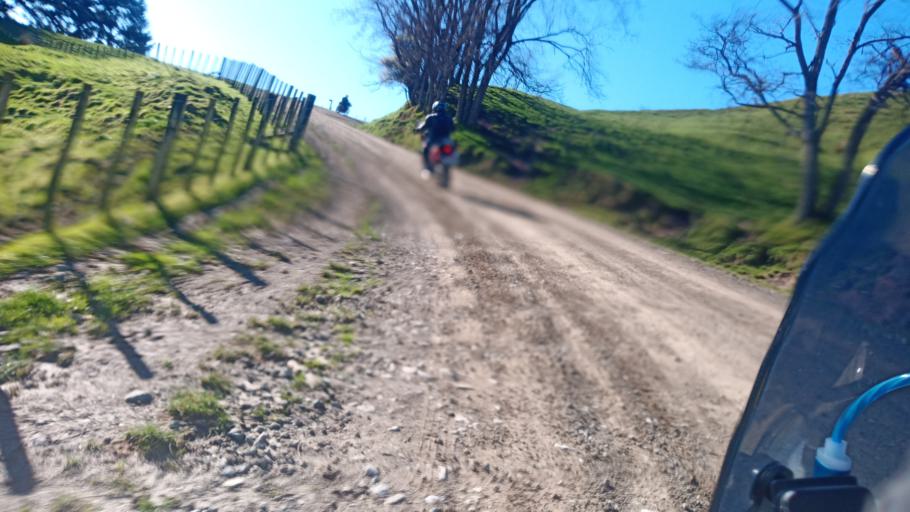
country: NZ
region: Gisborne
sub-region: Gisborne District
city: Gisborne
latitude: -38.2922
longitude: 177.8867
